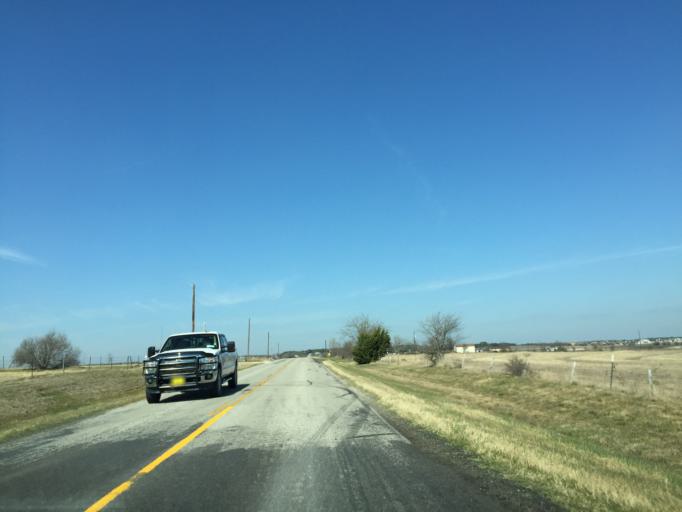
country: US
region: Texas
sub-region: Williamson County
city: Serenada
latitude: 30.7208
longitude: -97.5814
